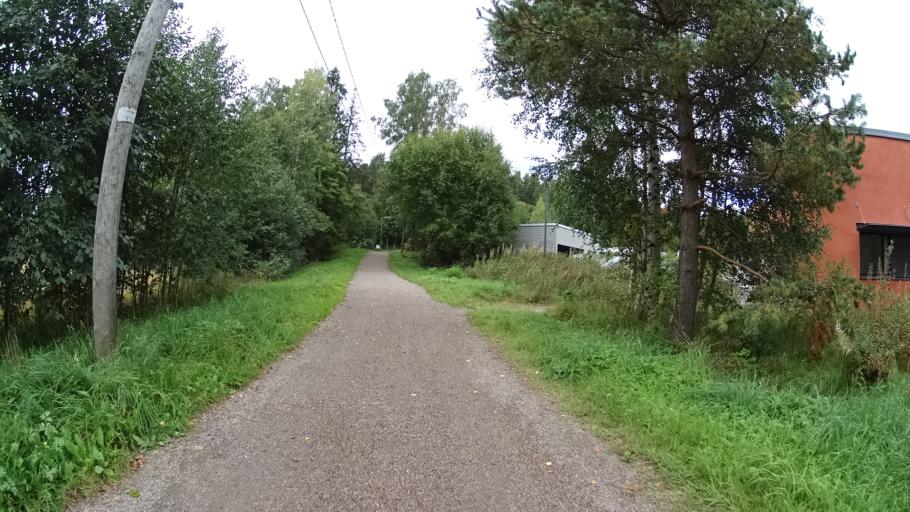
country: FI
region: Uusimaa
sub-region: Helsinki
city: Espoo
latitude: 60.2252
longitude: 24.6878
